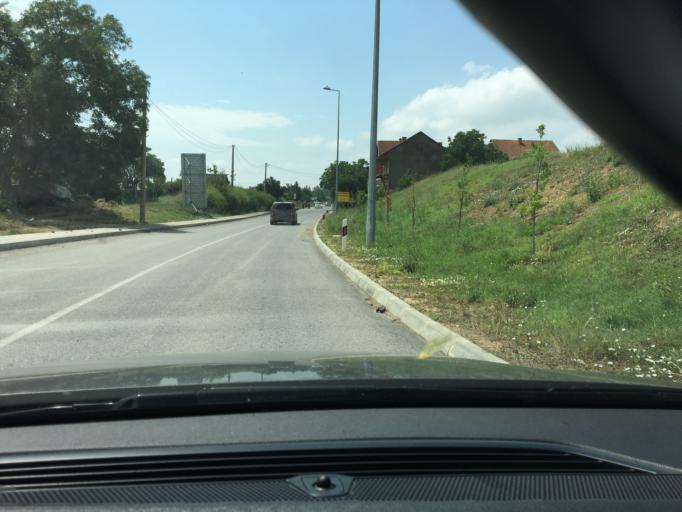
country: MK
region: Sveti Nikole
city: Sveti Nikole
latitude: 41.8756
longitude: 21.9387
